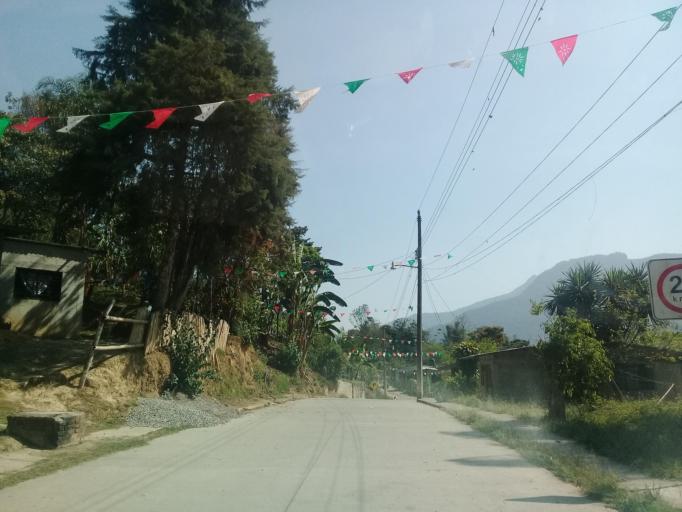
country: MX
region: Veracruz
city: Rafael Delgado
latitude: 18.7820
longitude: -97.0190
